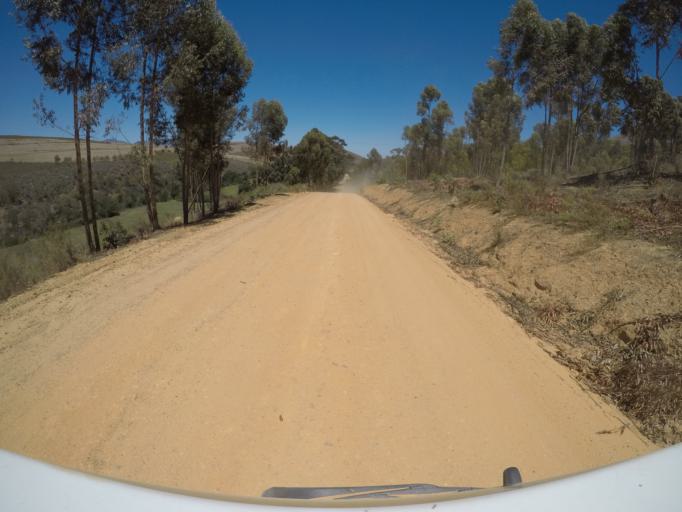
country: ZA
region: Western Cape
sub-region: Overberg District Municipality
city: Caledon
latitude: -34.1990
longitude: 19.2209
